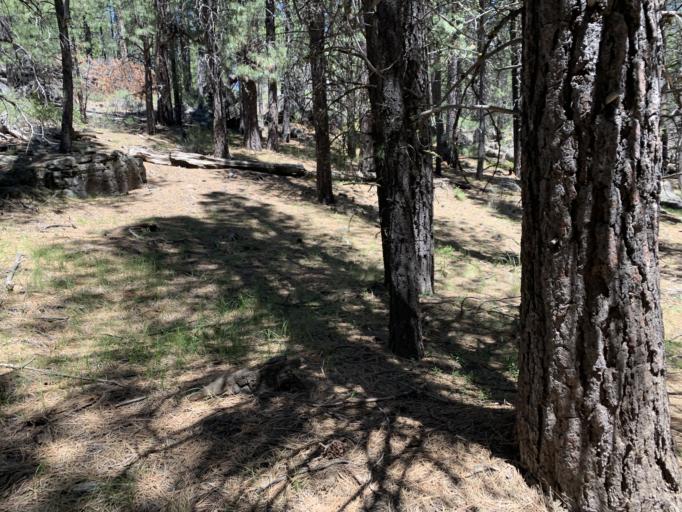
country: US
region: Oregon
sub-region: Deschutes County
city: Deschutes River Woods
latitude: 44.0151
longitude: -121.4270
